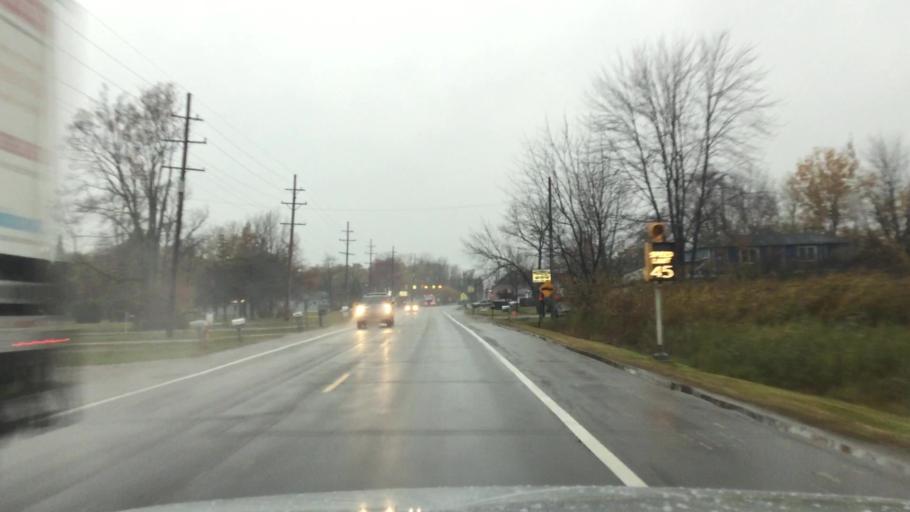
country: US
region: Michigan
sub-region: Saint Clair County
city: Pearl Beach
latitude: 42.6232
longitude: -82.5819
